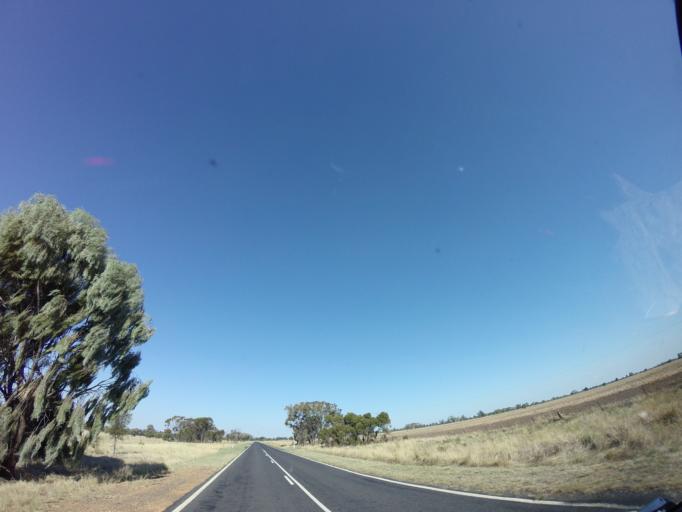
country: AU
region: New South Wales
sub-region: Gilgandra
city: Gilgandra
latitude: -31.6629
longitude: 148.3888
